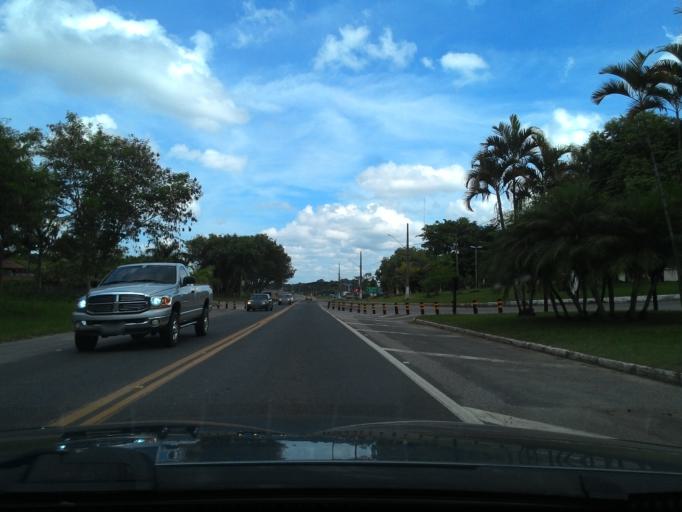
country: BR
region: Sao Paulo
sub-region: Registro
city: Registro
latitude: -24.5047
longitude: -47.8527
